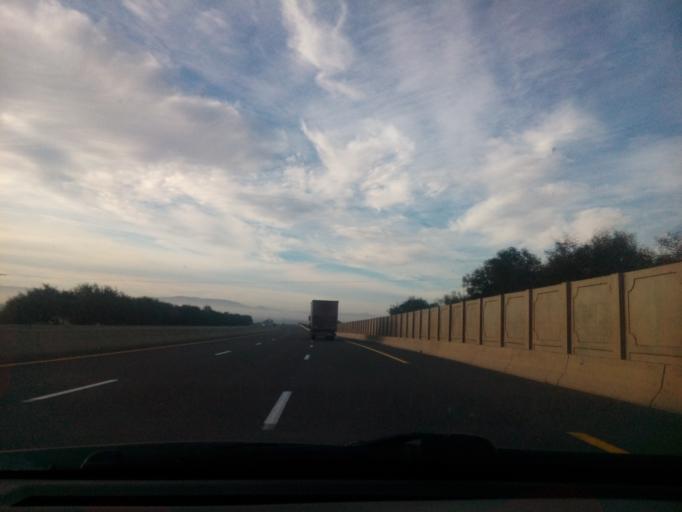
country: DZ
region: Relizane
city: Relizane
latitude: 35.7277
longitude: 0.3025
